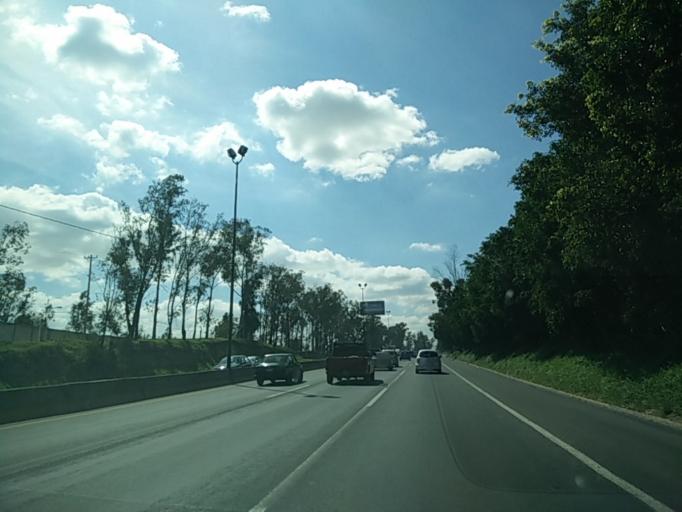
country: MX
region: Jalisco
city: Zapopan2
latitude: 20.7171
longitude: -103.4276
